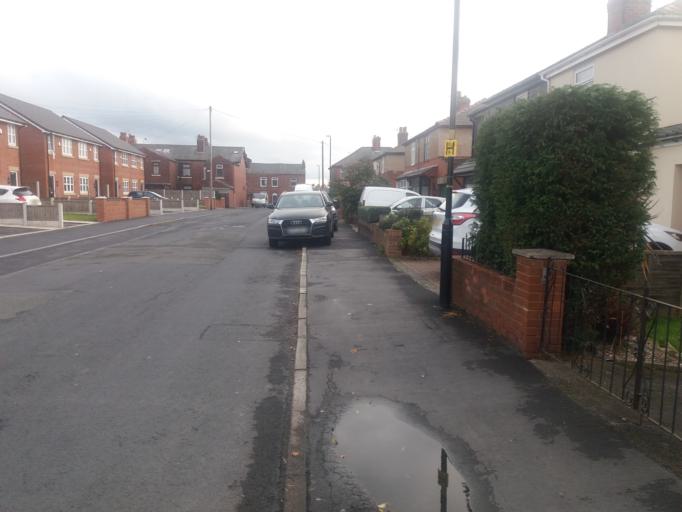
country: GB
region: England
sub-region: Lancashire
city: Chorley
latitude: 53.6624
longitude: -2.6204
